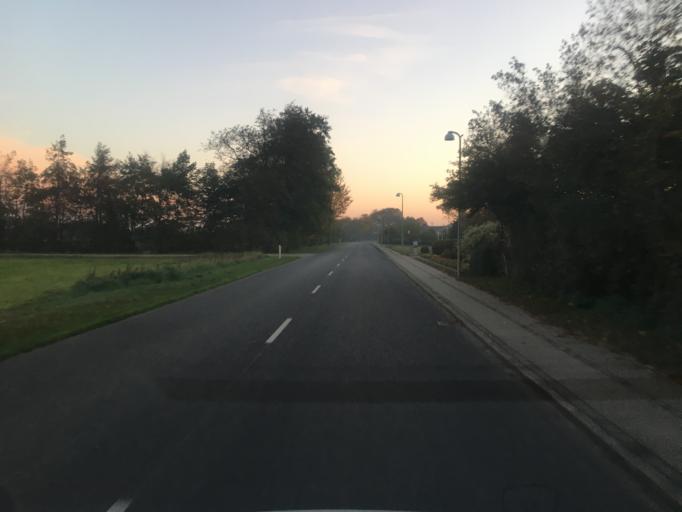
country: DE
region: Schleswig-Holstein
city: Bramstedtlund
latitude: 54.9465
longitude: 9.0927
